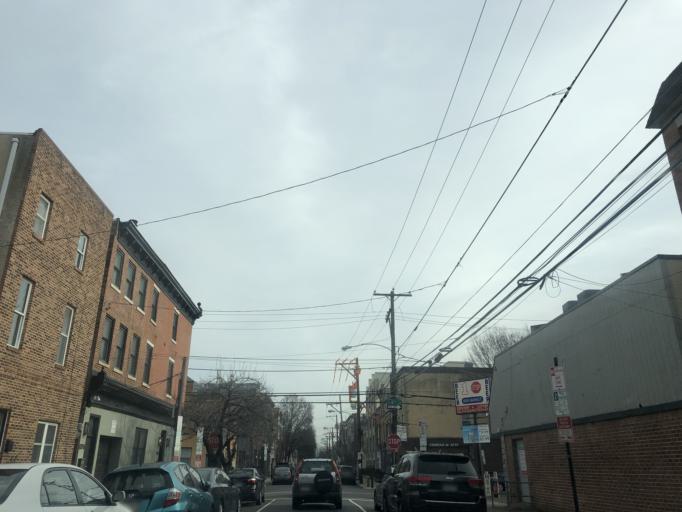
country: US
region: Pennsylvania
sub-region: Philadelphia County
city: Philadelphia
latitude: 39.9416
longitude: -75.1562
